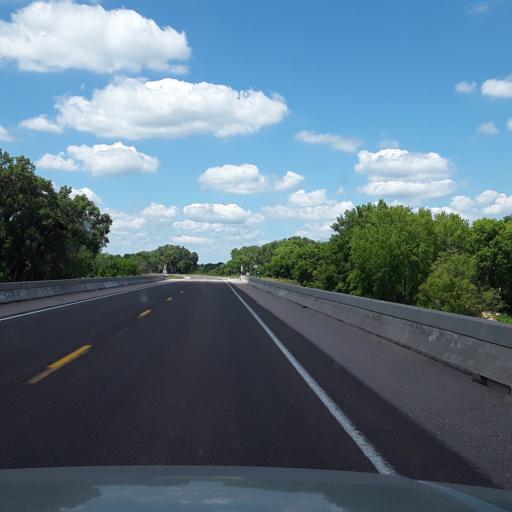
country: US
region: Nebraska
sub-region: Nance County
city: Genoa
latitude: 41.4185
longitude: -97.7236
